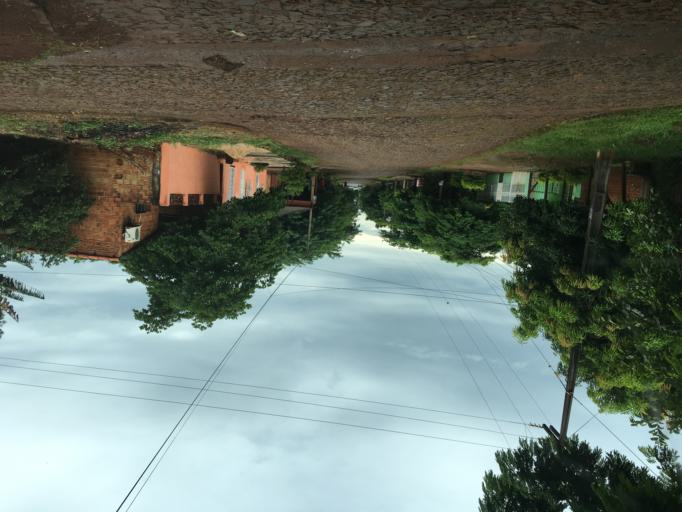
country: PY
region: Alto Parana
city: Ciudad del Este
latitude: -25.4335
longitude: -54.6452
